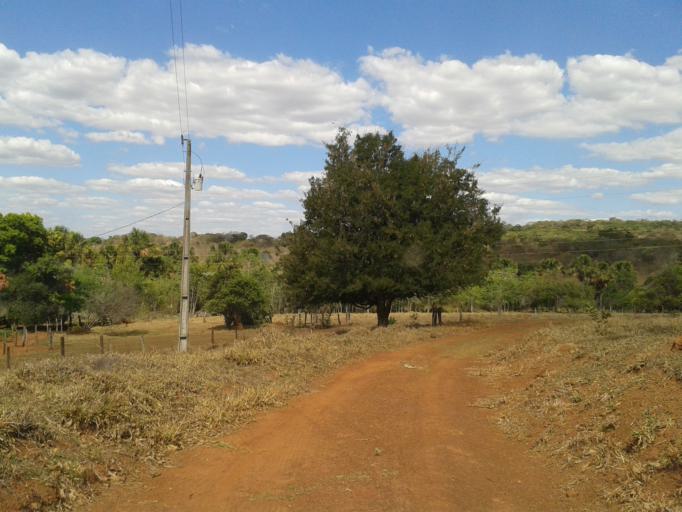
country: BR
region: Minas Gerais
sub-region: Monte Alegre De Minas
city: Monte Alegre de Minas
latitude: -18.7909
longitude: -49.0941
